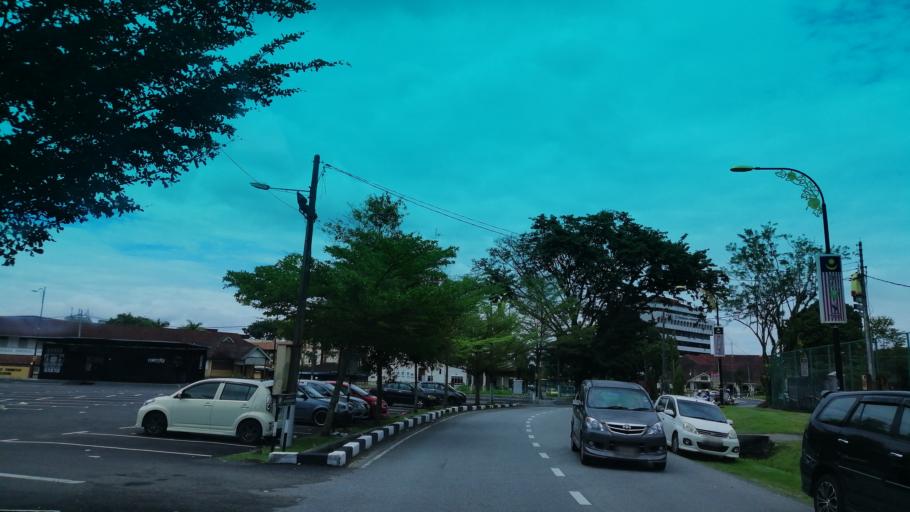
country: MY
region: Perak
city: Taiping
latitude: 4.8535
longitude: 100.7462
